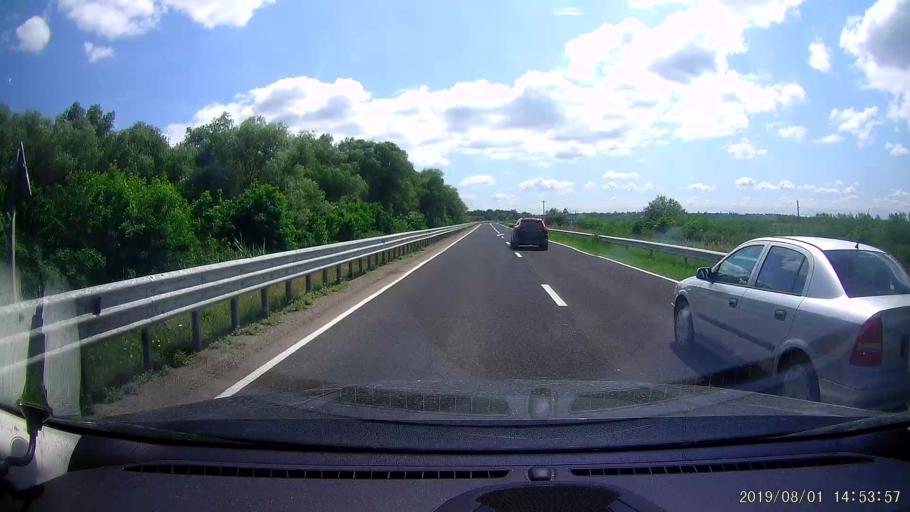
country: RO
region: Braila
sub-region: Municipiul Braila
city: Braila
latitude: 45.3260
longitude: 27.9970
